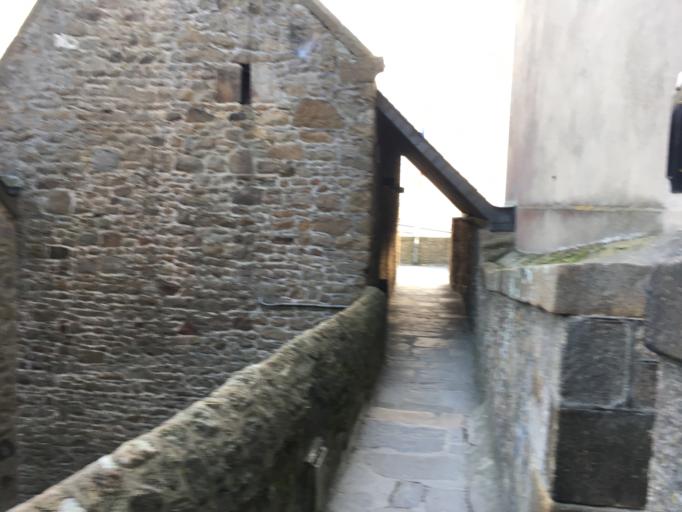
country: FR
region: Lower Normandy
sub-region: Departement de la Manche
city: Pontorson
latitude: 48.6351
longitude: -1.5108
